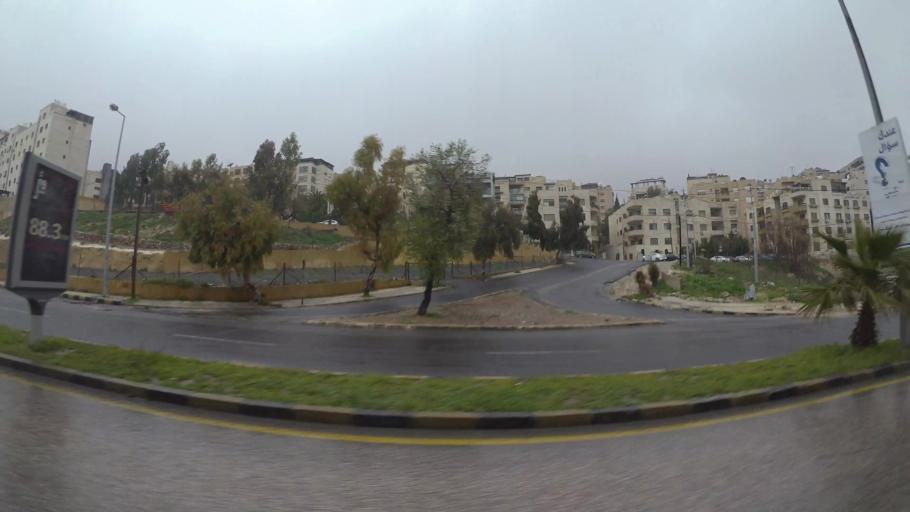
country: JO
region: Amman
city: Amman
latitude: 31.9604
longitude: 35.8945
